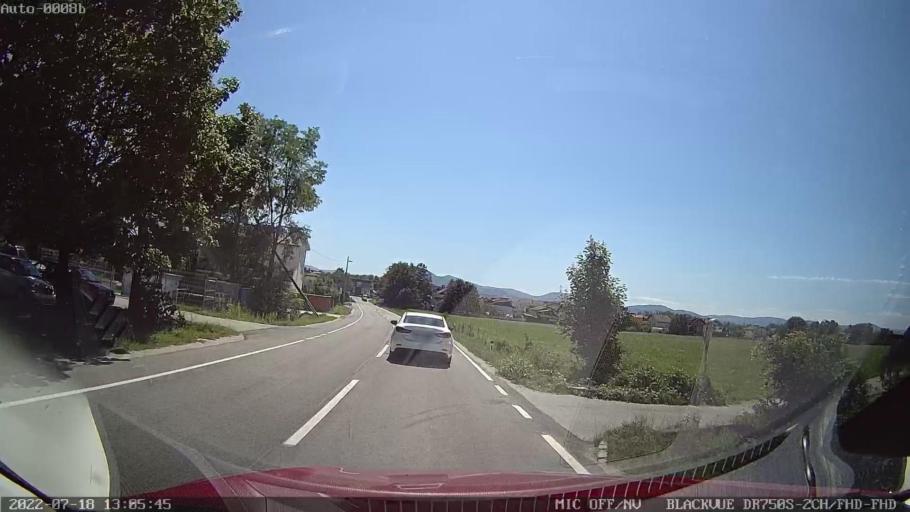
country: SI
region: Brezovica
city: Vnanje Gorice
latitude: 46.0336
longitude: 14.4428
